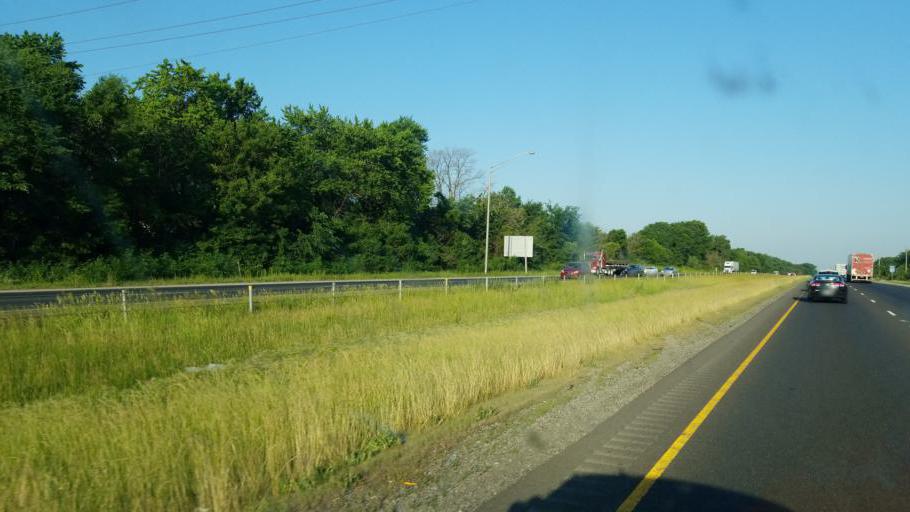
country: US
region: Illinois
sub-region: Will County
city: Ingalls Park
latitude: 41.5131
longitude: -88.0474
